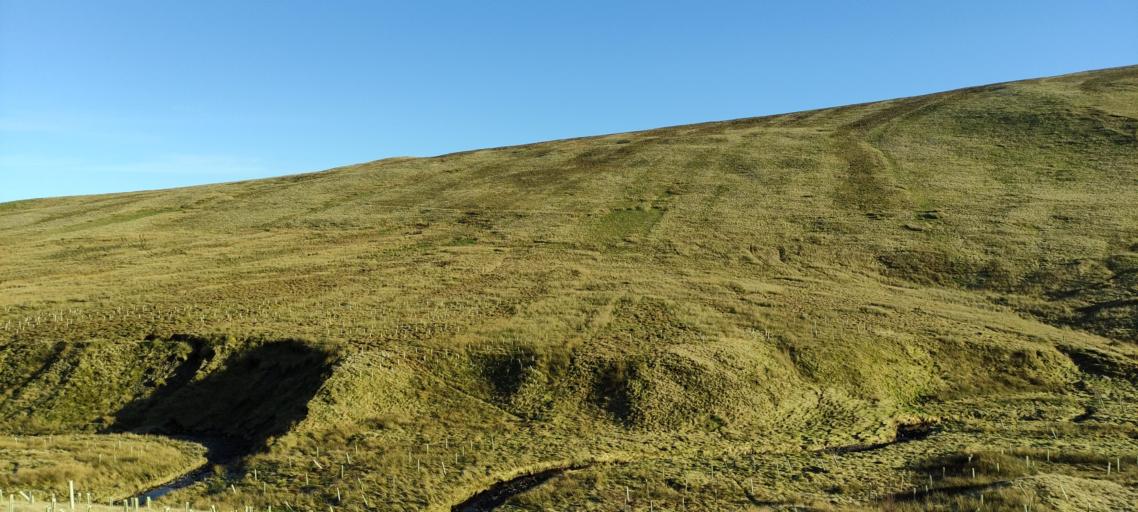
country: GB
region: England
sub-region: Cumbria
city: Sedbergh
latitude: 54.4135
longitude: -2.5666
